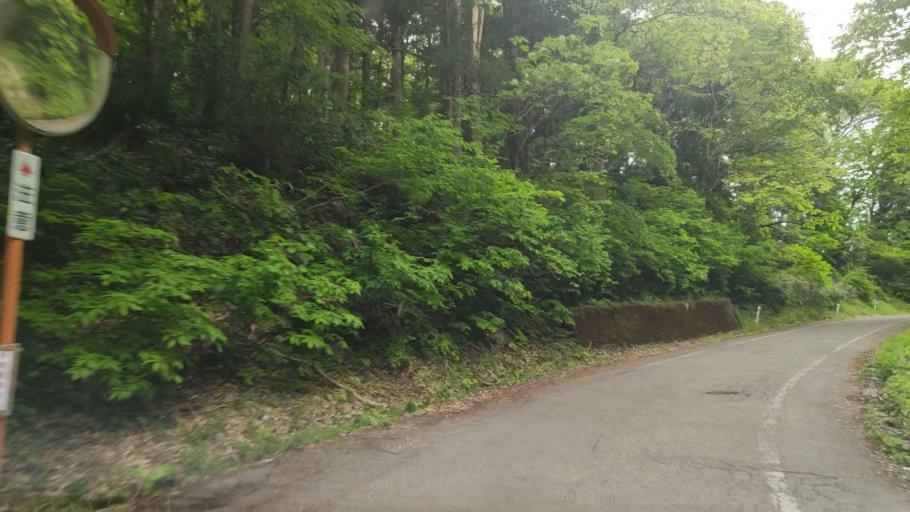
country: JP
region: Niigata
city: Kamo
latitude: 37.7151
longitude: 139.0905
